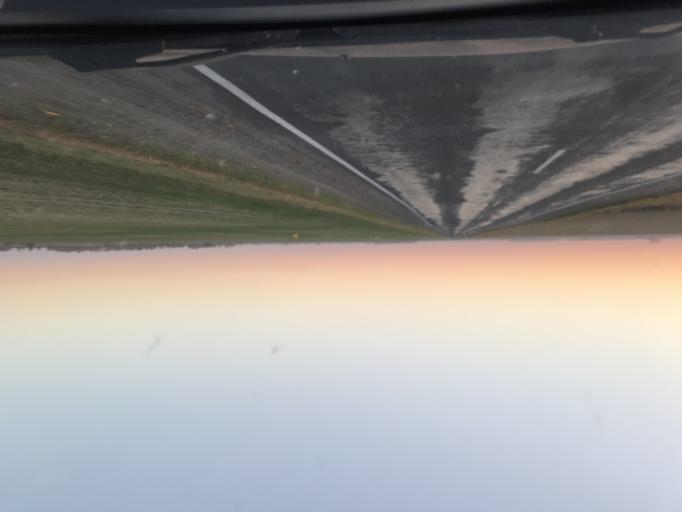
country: BY
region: Gomel
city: Horad Rechytsa
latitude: 52.1627
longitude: 30.5850
